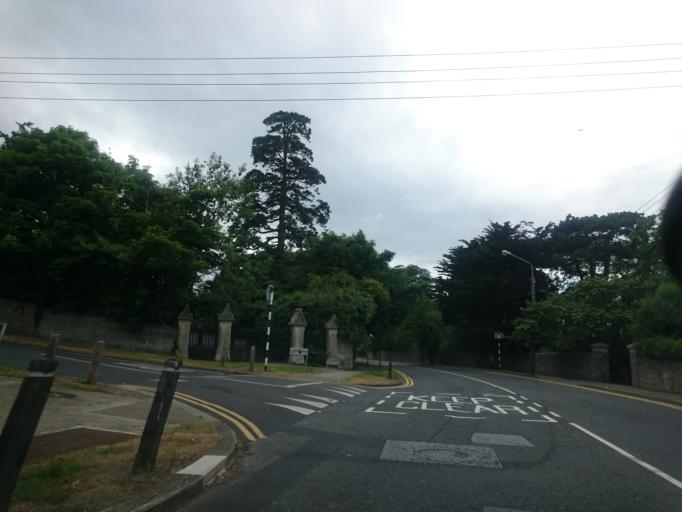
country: IE
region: Leinster
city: Balally
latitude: 53.2916
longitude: -6.2374
